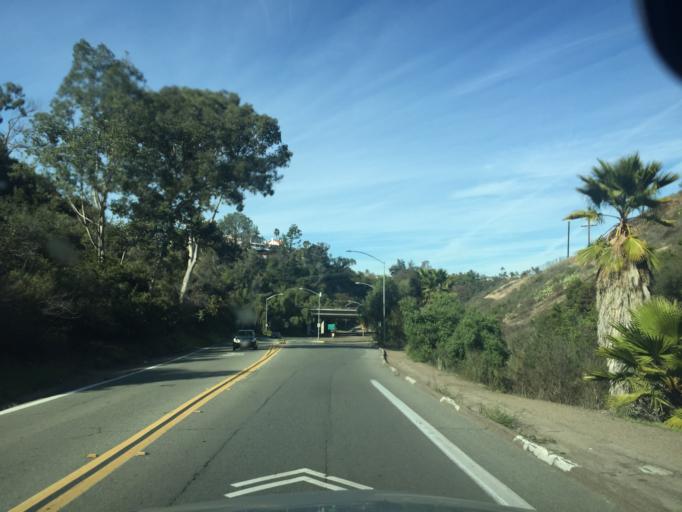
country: US
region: California
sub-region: San Diego County
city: Lemon Grove
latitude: 32.7612
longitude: -117.0963
